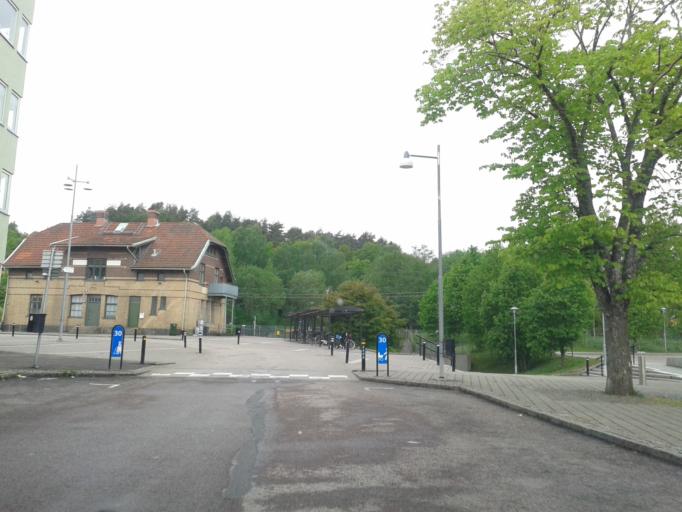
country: SE
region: Vaestra Goetaland
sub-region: Kungalvs Kommun
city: Kungalv
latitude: 57.8625
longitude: 11.9191
